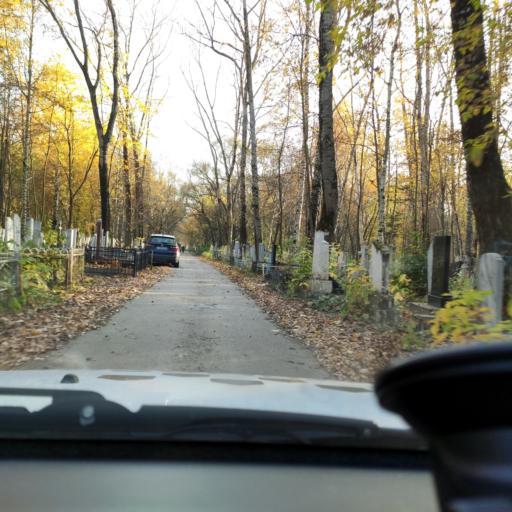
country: RU
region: Perm
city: Perm
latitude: 57.9911
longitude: 56.2814
